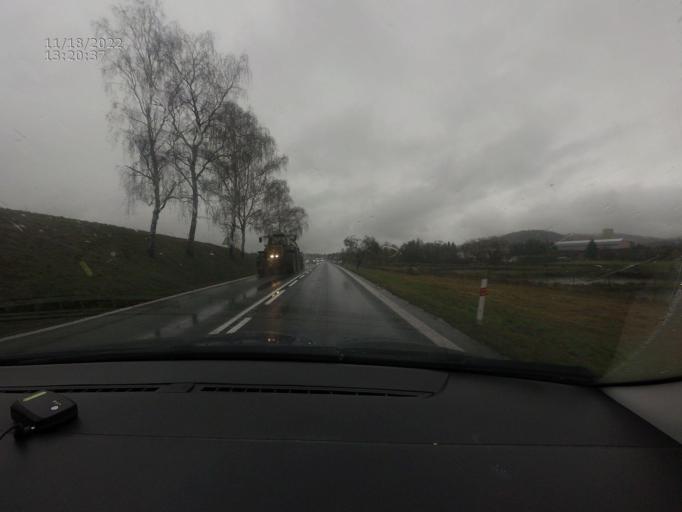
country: CZ
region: Plzensky
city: Horazd'ovice
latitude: 49.3273
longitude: 13.6752
